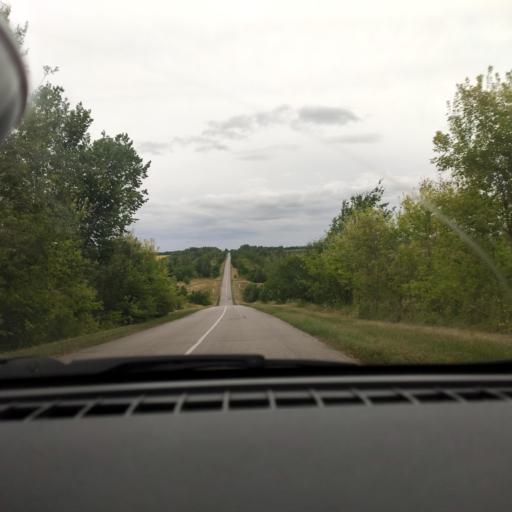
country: RU
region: Samara
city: Georgiyevka
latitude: 53.5153
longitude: 51.0000
